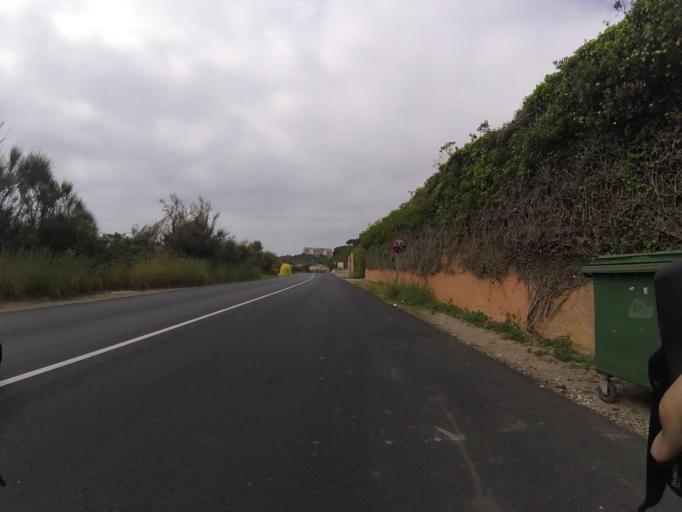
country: ES
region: Valencia
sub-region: Provincia de Castello
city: Peniscola
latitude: 40.3491
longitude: 0.3911
